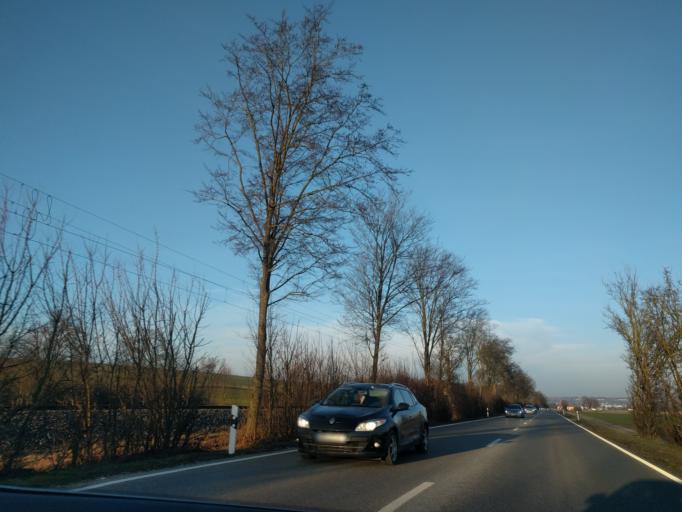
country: DE
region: Bavaria
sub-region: Swabia
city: Tapfheim
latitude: 48.6928
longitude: 10.7321
